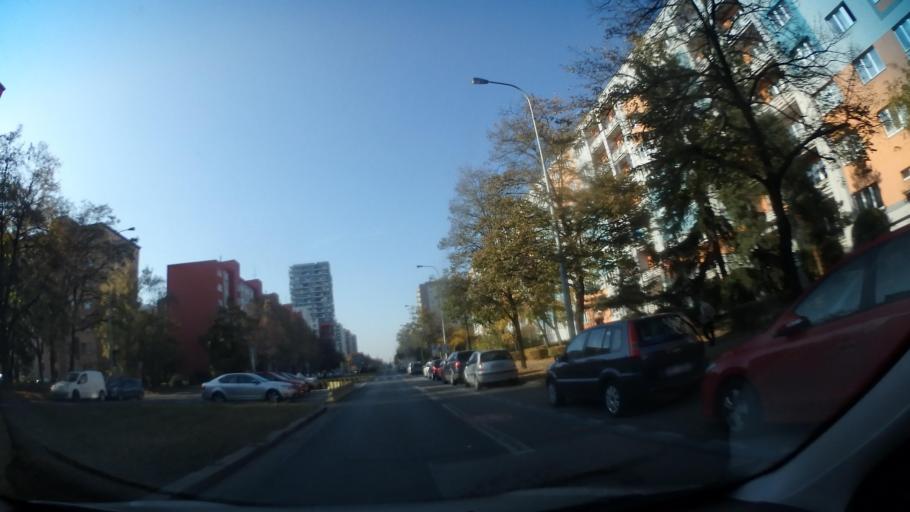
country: CZ
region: Praha
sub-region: Praha 9
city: Vysocany
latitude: 50.0824
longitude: 14.5036
